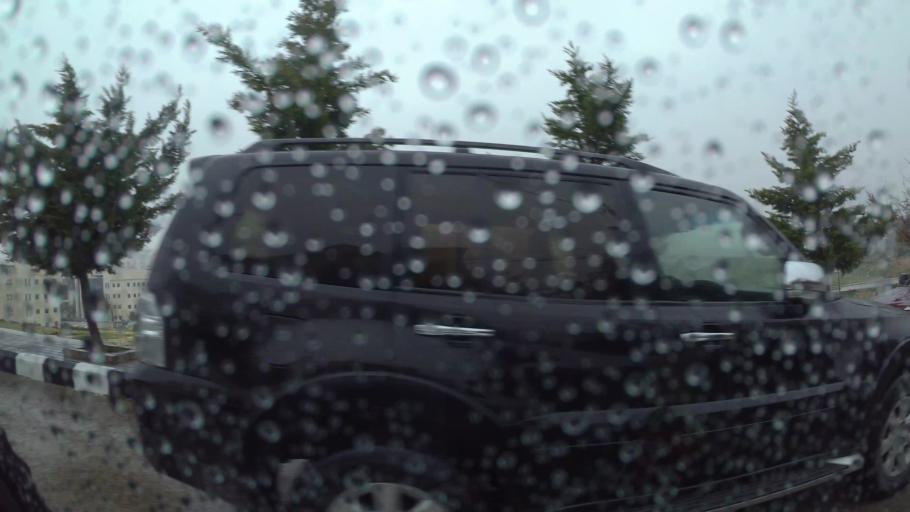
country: JO
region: Amman
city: Al Jubayhah
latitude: 32.0069
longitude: 35.8311
